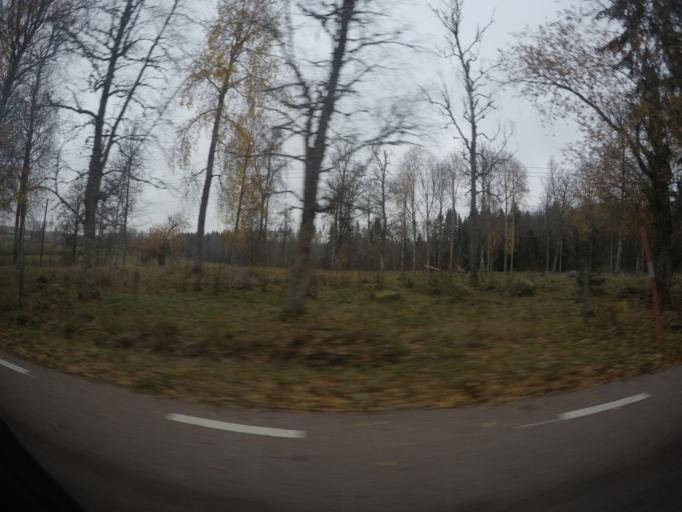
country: SE
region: Vaestmanland
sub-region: Surahammars Kommun
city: Ramnas
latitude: 59.6937
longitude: 16.0783
